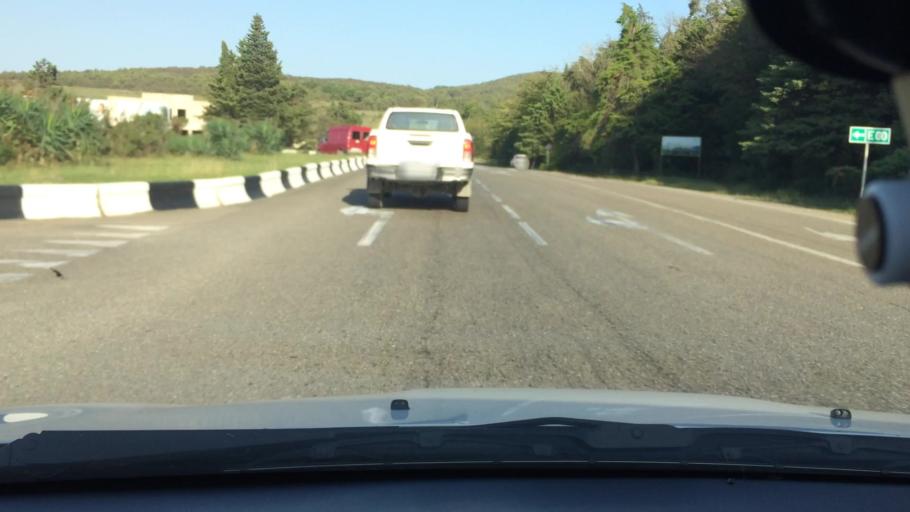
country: GE
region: Imereti
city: Kutaisi
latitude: 42.2395
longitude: 42.7664
